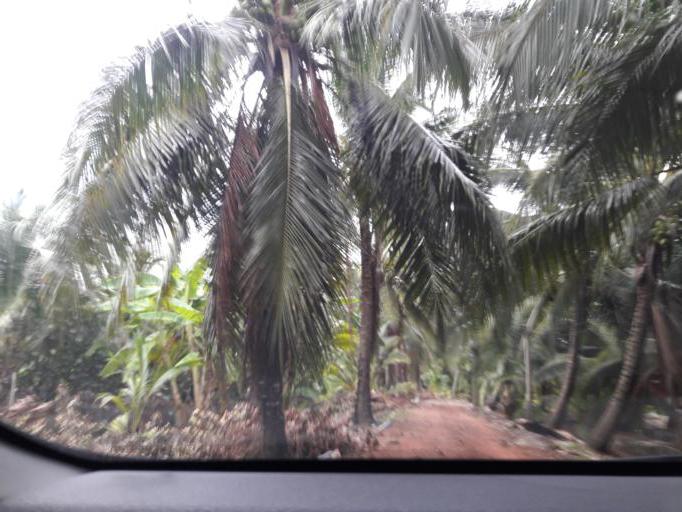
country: TH
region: Ratchaburi
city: Damnoen Saduak
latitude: 13.5595
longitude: 99.9854
